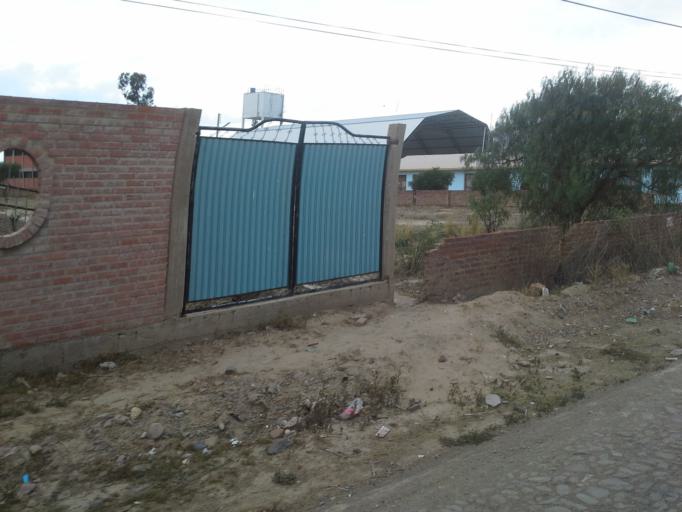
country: BO
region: Cochabamba
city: Tarata
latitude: -17.5860
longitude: -66.0171
